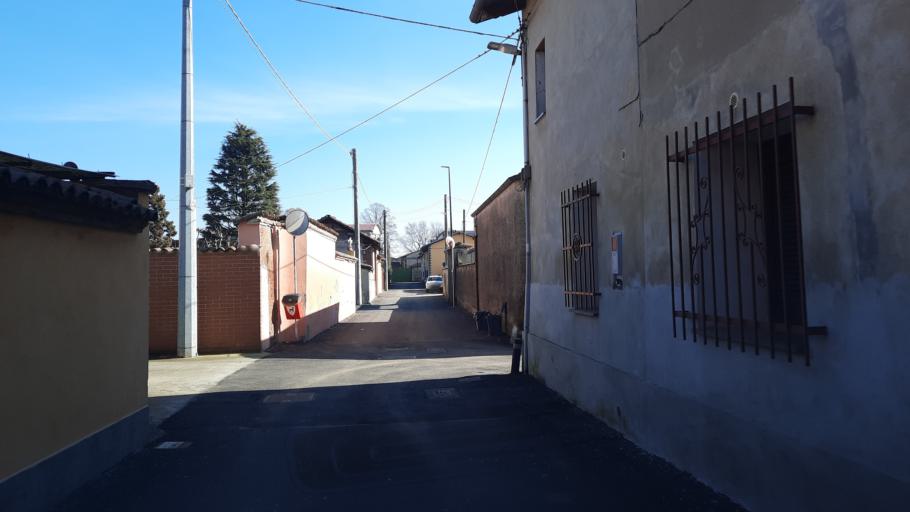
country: IT
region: Piedmont
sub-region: Provincia di Vercelli
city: Pertengo
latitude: 45.2348
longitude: 8.4164
